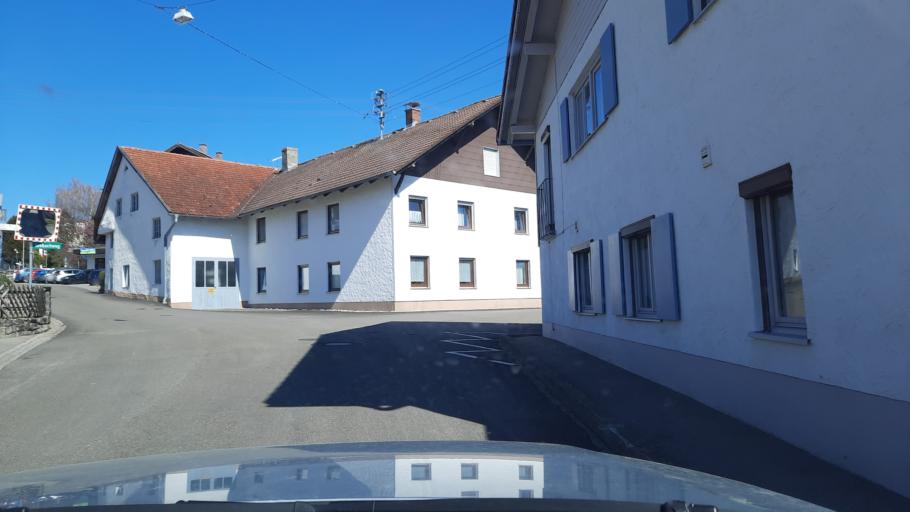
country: DE
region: Bavaria
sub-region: Swabia
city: Haldenwang
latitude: 47.8172
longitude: 10.3318
